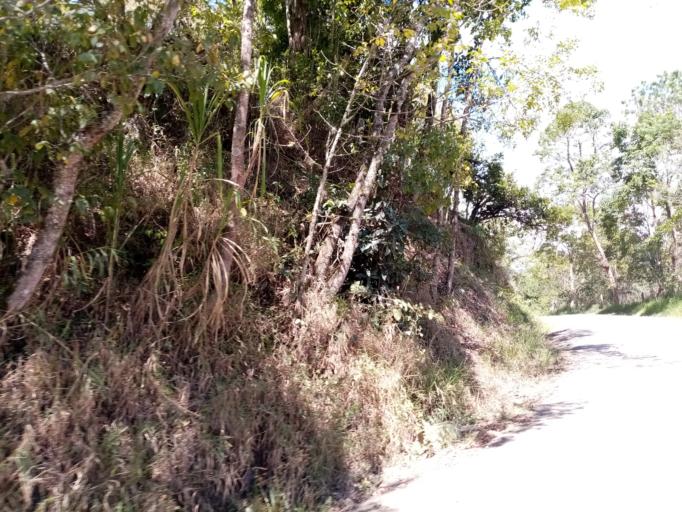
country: CO
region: Cundinamarca
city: Tenza
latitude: 5.0764
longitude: -73.4256
